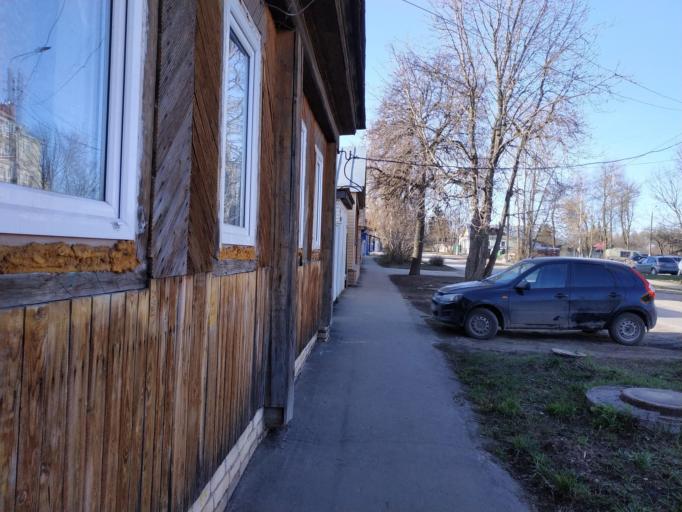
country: RU
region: Nizjnij Novgorod
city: Arzamas
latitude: 55.3953
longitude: 43.8144
